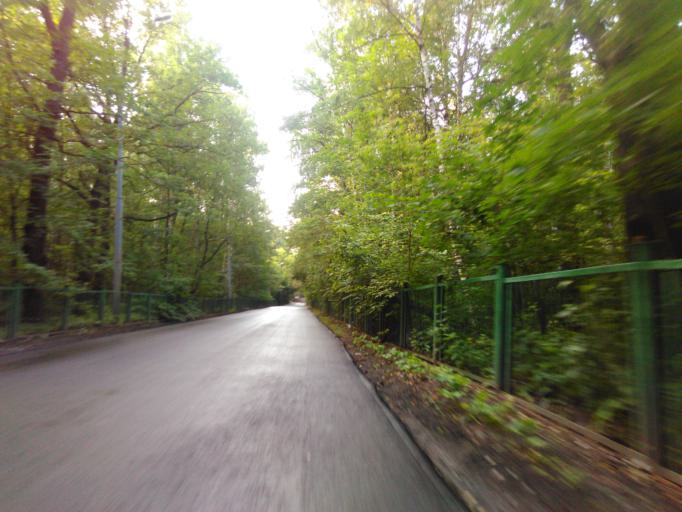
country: RU
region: Moskovskaya
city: Bogorodskoye
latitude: 55.8283
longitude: 37.6943
